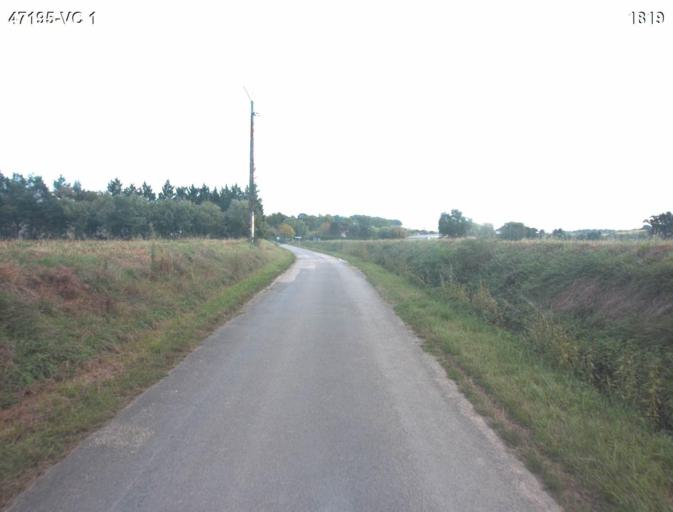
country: FR
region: Aquitaine
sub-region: Departement du Lot-et-Garonne
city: Nerac
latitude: 44.1205
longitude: 0.3524
